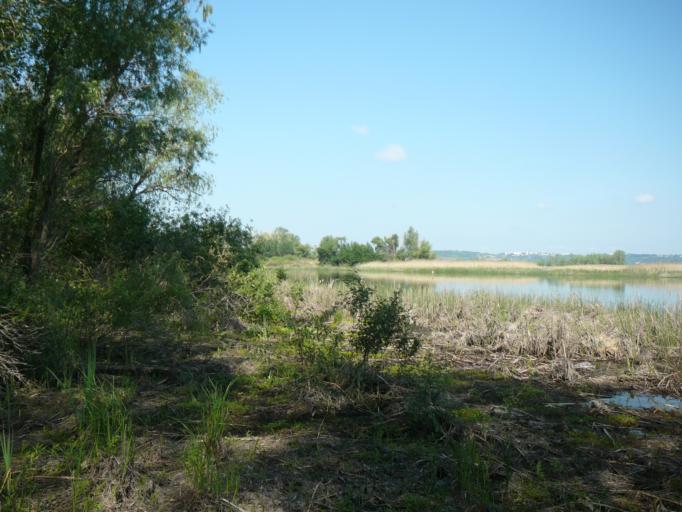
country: RU
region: Saratov
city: Engel's
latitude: 51.5120
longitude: 46.1431
